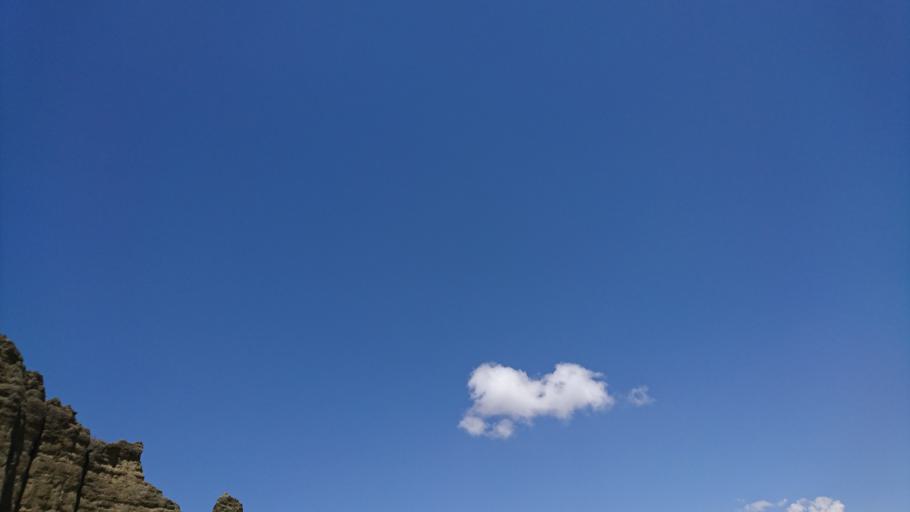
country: BO
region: La Paz
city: La Paz
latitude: -16.5387
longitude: -68.0116
